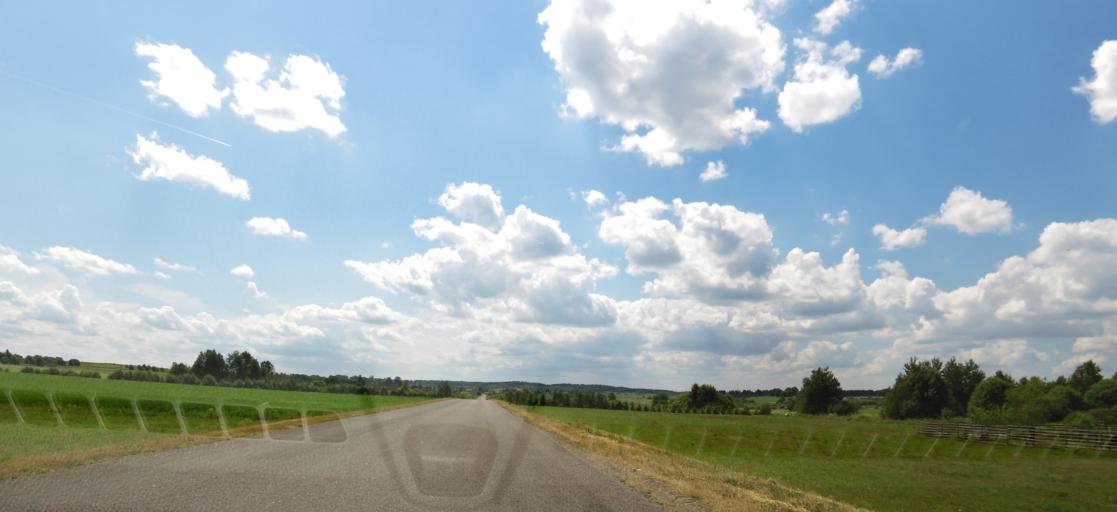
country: LT
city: Skaidiskes
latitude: 54.5530
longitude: 25.6606
